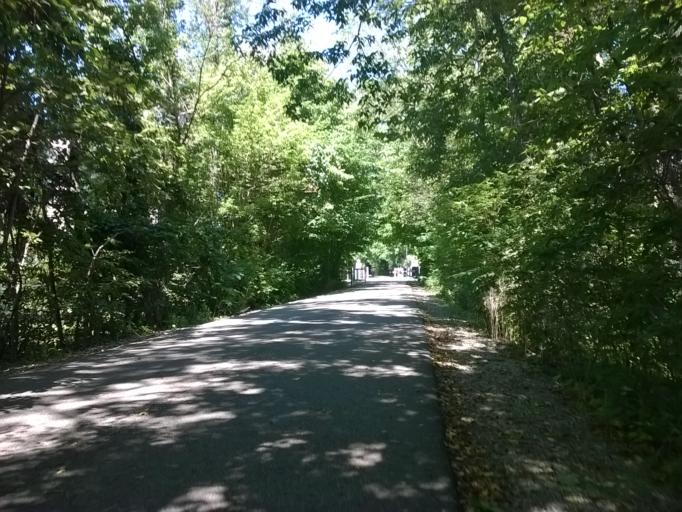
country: US
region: Indiana
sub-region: Hamilton County
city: Carmel
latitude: 39.9847
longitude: -86.1300
